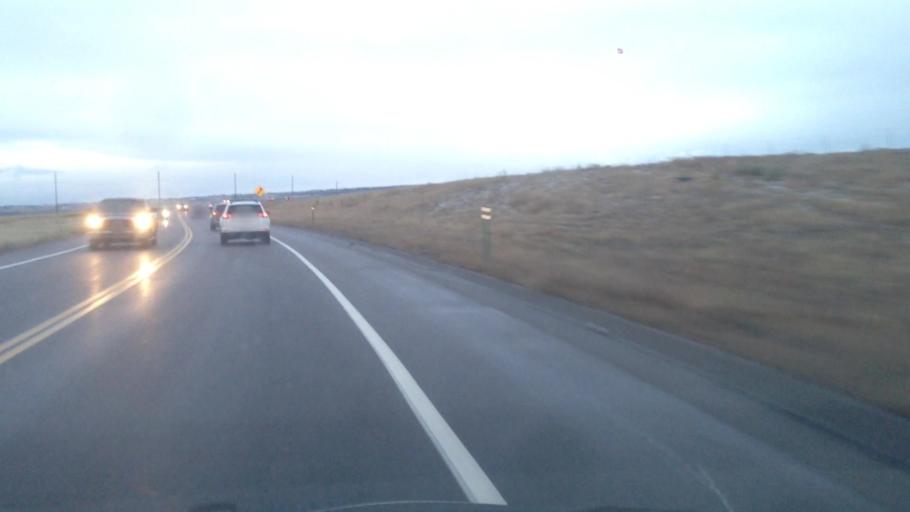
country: US
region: Colorado
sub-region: Douglas County
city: Meridian
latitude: 39.5199
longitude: -104.8439
